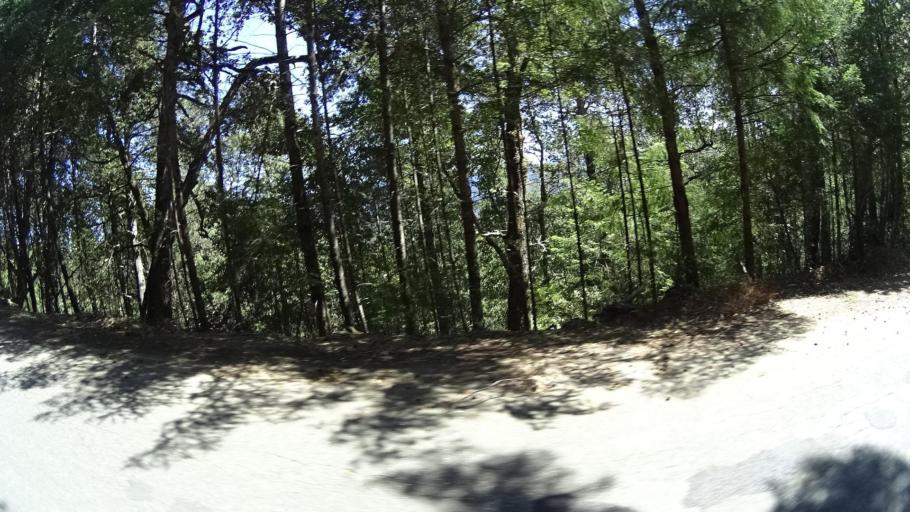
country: US
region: California
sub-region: Humboldt County
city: Redway
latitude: 40.1551
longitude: -124.0709
